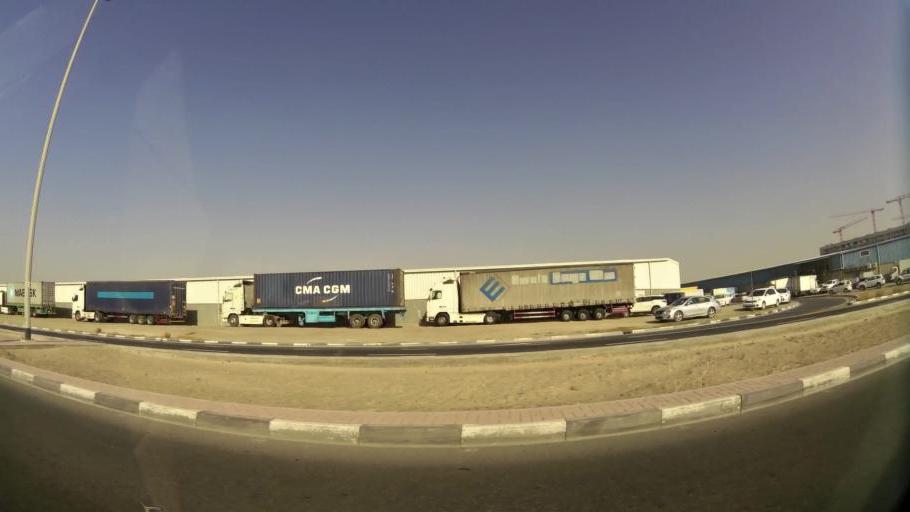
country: AE
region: Ash Shariqah
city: Sharjah
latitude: 25.2848
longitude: 55.3809
